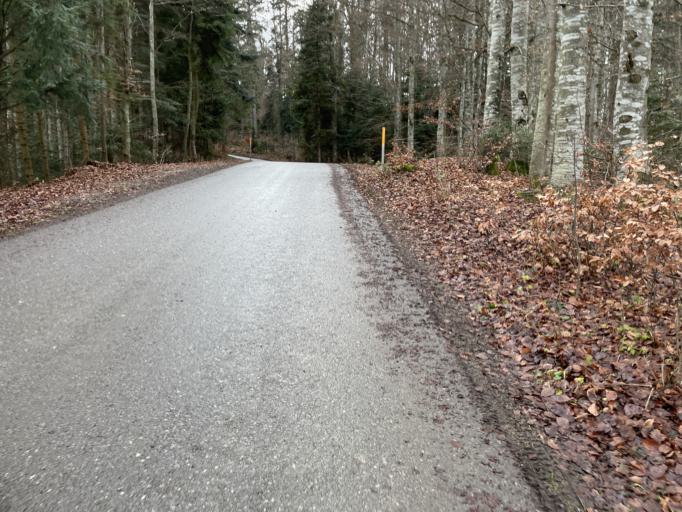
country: CH
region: Bern
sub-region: Bern-Mittelland District
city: Toffen
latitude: 46.8646
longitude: 7.5193
